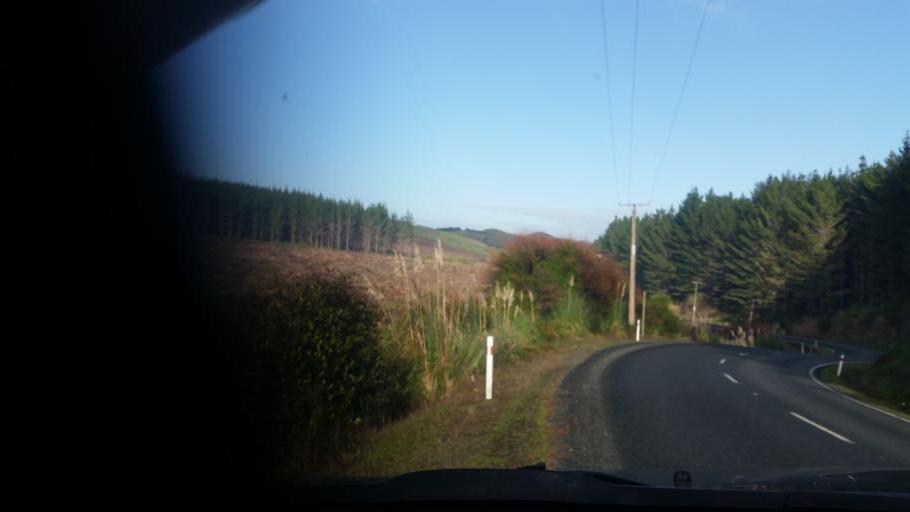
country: NZ
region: Auckland
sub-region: Auckland
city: Wellsford
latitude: -36.2164
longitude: 174.4673
